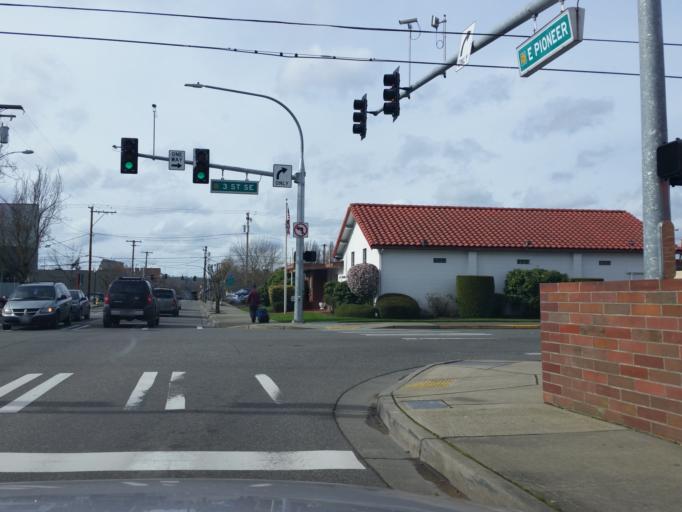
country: US
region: Washington
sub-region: Pierce County
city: Puyallup
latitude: 47.1905
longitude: -122.2910
